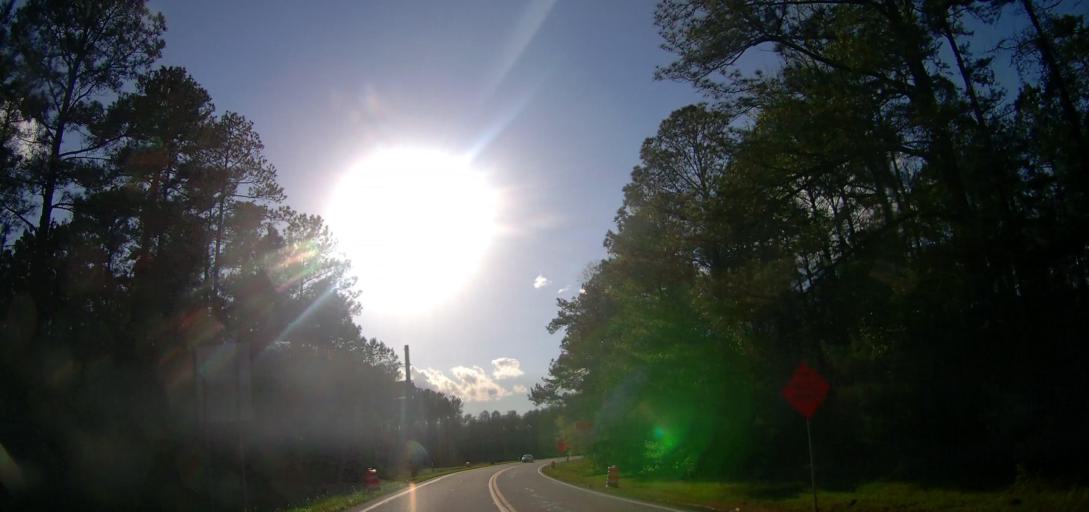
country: US
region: Georgia
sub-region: Baldwin County
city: Milledgeville
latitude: 33.1270
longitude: -83.3126
